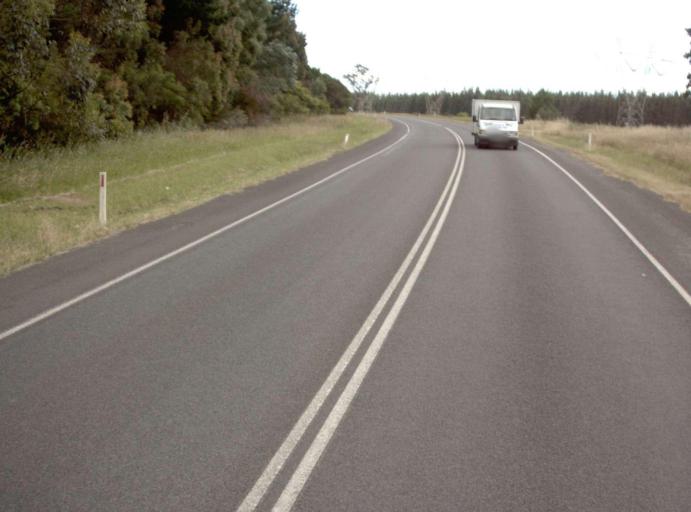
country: AU
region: Victoria
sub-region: Latrobe
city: Morwell
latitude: -38.1964
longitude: 146.4486
